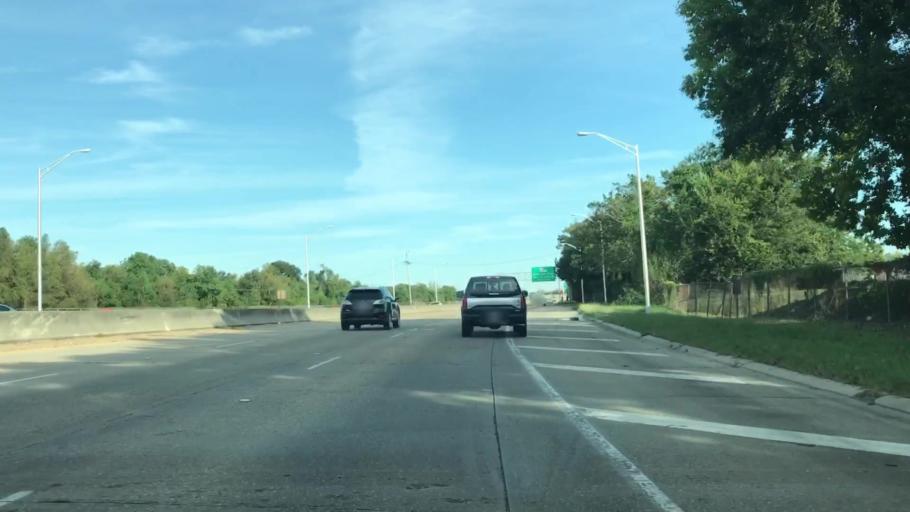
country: US
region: Louisiana
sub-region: Jefferson Parish
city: Elmwood
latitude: 29.9690
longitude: -90.1963
